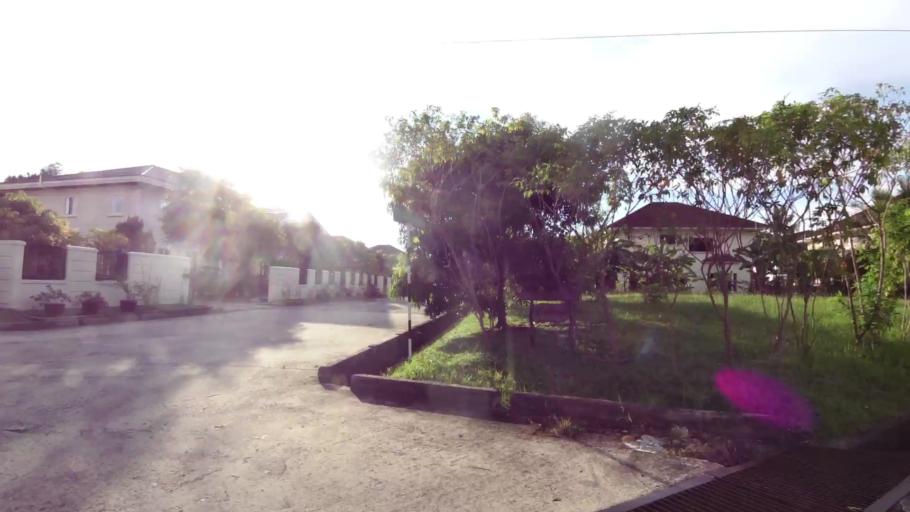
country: BN
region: Brunei and Muara
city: Bandar Seri Begawan
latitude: 4.9754
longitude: 114.9826
